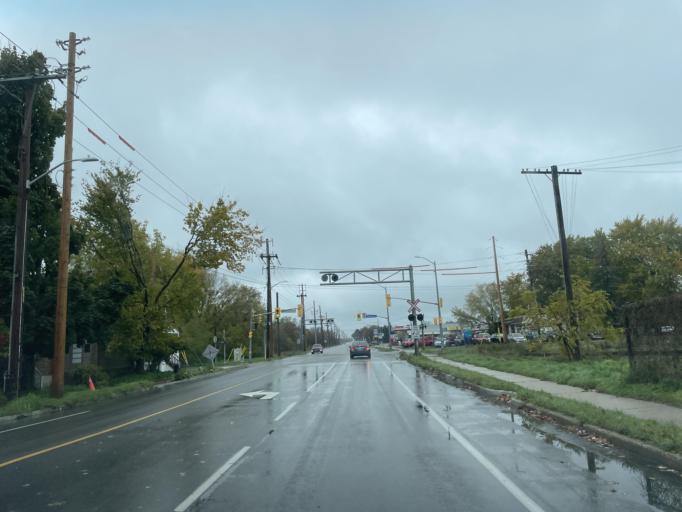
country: CA
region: Ontario
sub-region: Wellington County
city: Guelph
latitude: 43.5429
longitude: -80.2655
